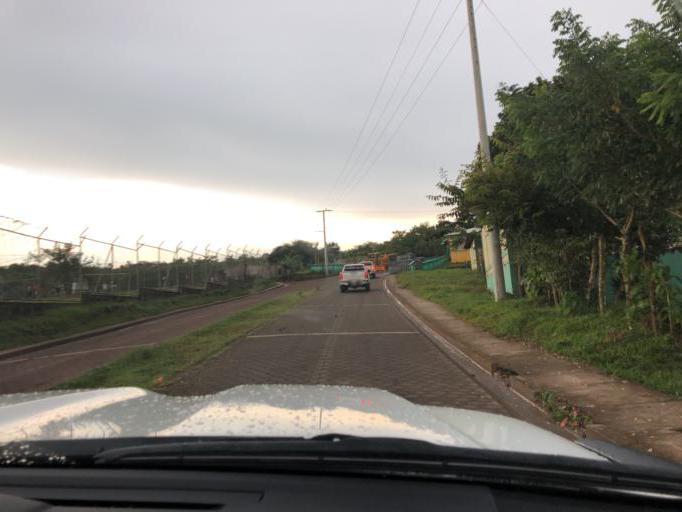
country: NI
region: Chontales
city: La Libertad
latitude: 12.2070
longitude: -85.1699
